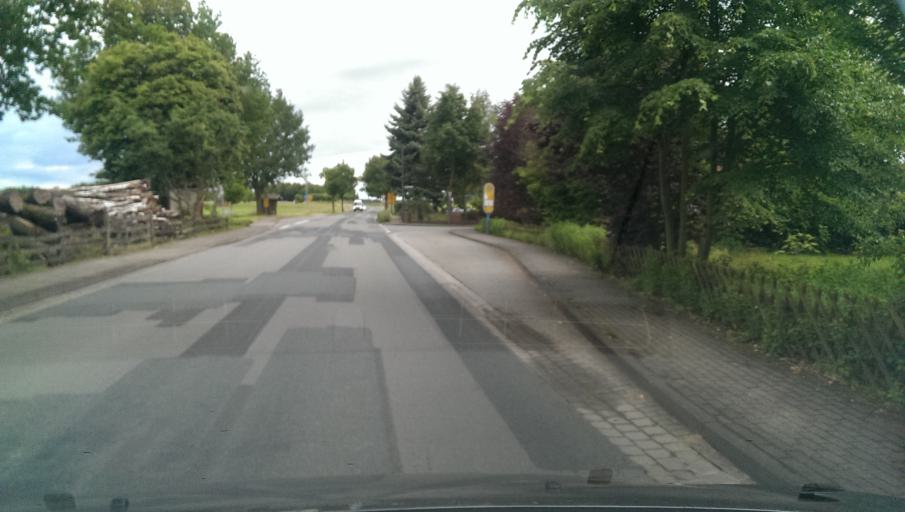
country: DE
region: Lower Saxony
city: Tulau
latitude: 52.6459
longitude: 10.8679
